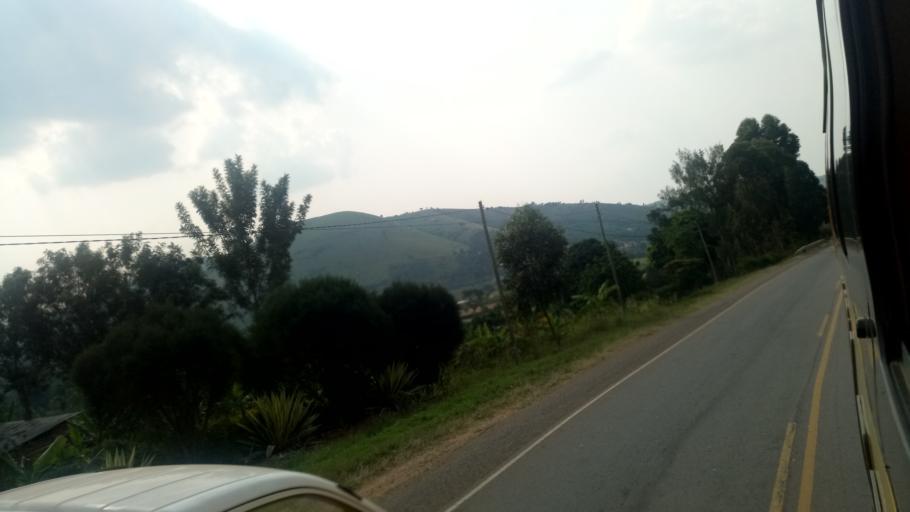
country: UG
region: Western Region
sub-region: Mbarara District
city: Mbarara
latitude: -0.5442
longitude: 30.7136
